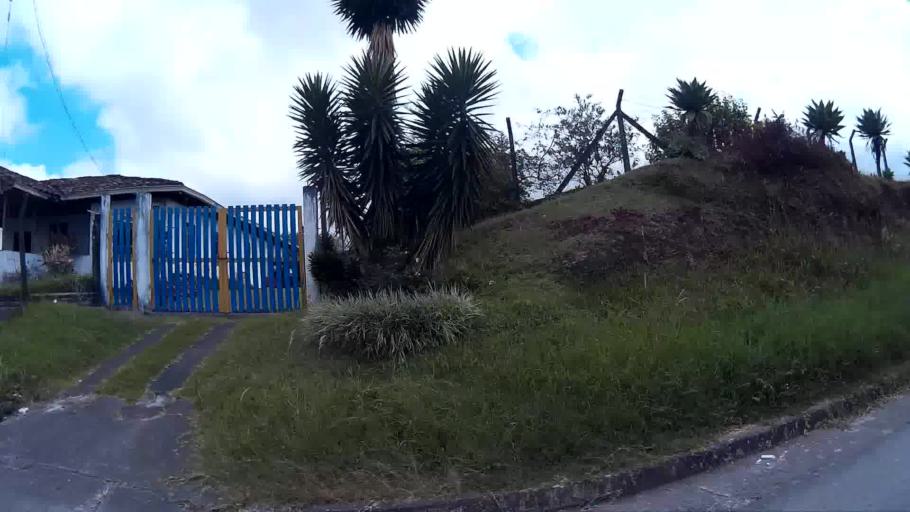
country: CO
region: Quindio
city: Circasia
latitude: 4.6234
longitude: -75.6231
